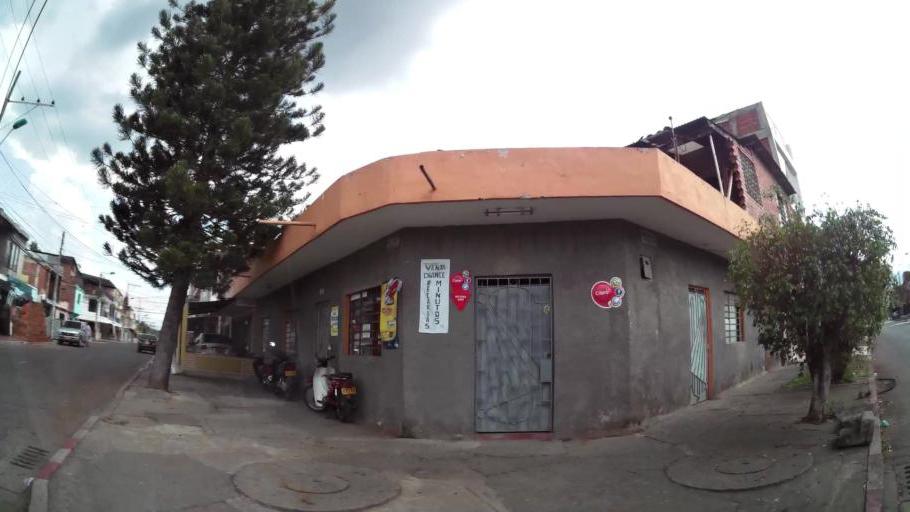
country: CO
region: Valle del Cauca
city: Cali
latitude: 3.4779
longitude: -76.5081
